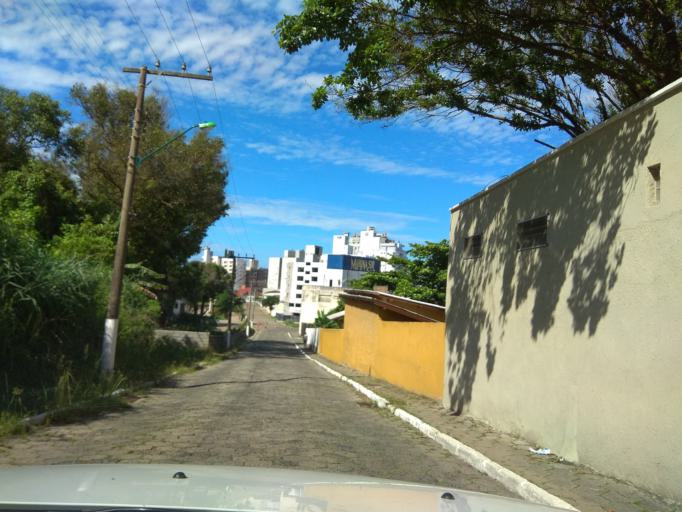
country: BR
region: Santa Catarina
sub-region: Laguna
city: Laguna
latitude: -28.4798
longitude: -48.7722
